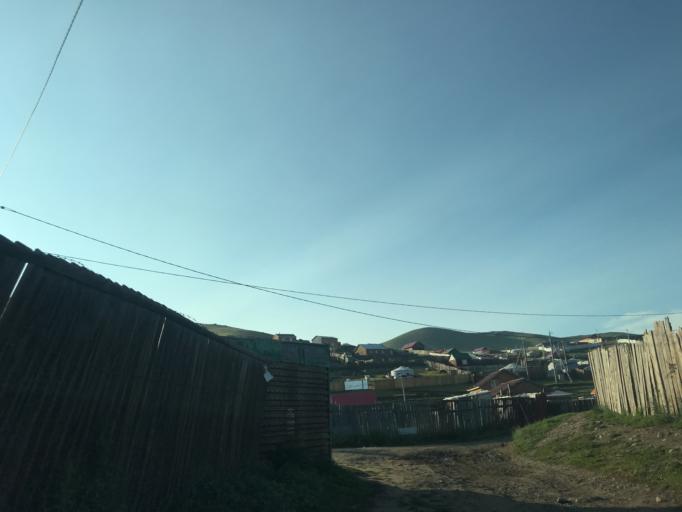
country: MN
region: Ulaanbaatar
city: Ulaanbaatar
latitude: 47.9886
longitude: 106.9619
